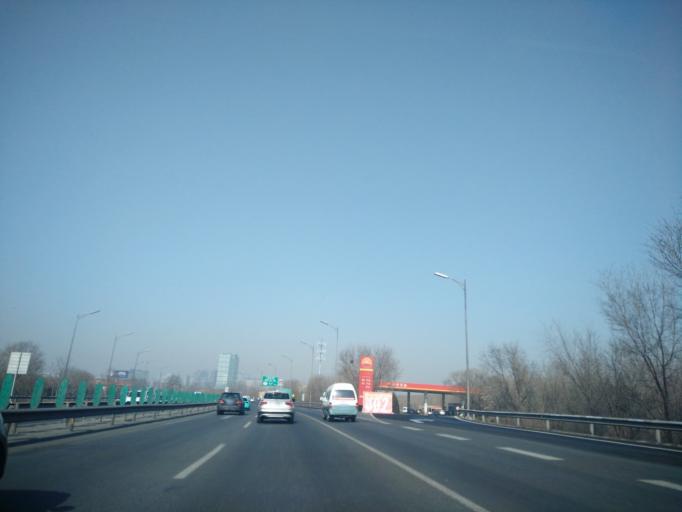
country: CN
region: Beijing
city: Wangjing
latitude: 40.0111
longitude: 116.4806
